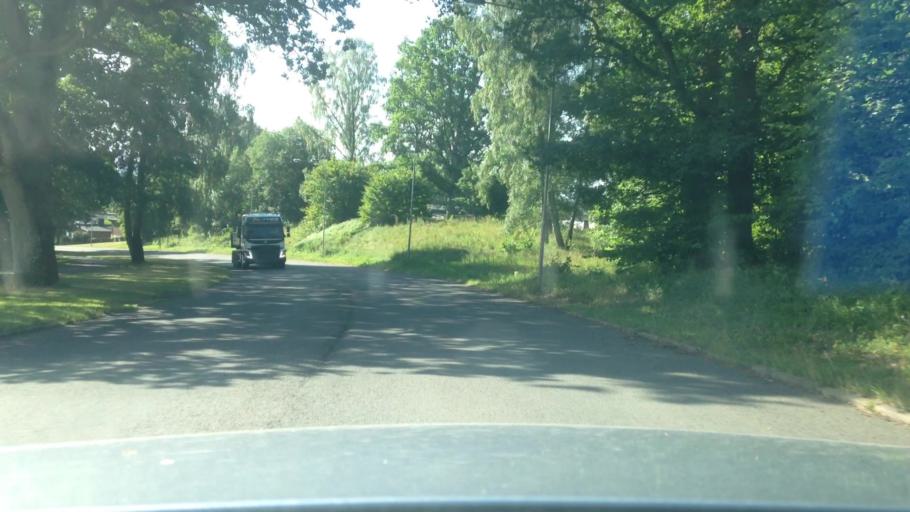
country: SE
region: Vaestra Goetaland
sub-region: Skovde Kommun
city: Skoevde
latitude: 58.3966
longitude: 13.8187
